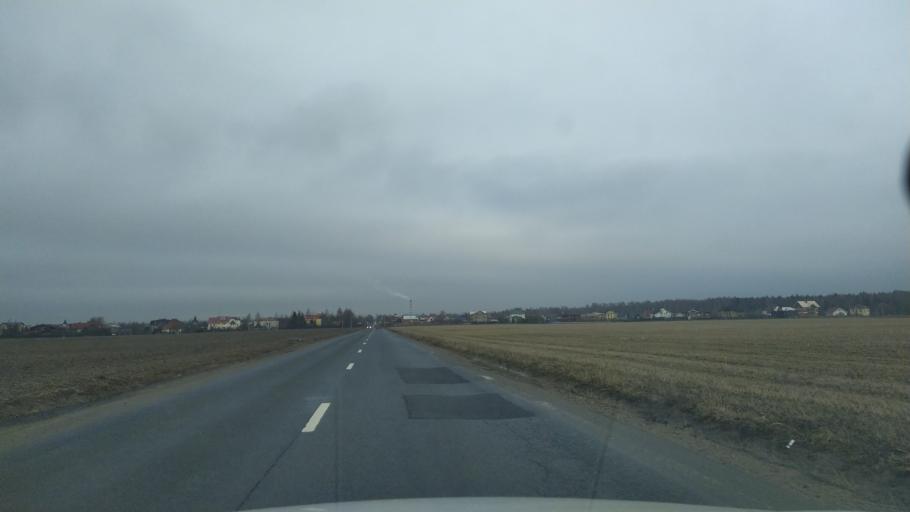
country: RU
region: St.-Petersburg
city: Aleksandrovskaya
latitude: 59.7188
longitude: 30.3410
